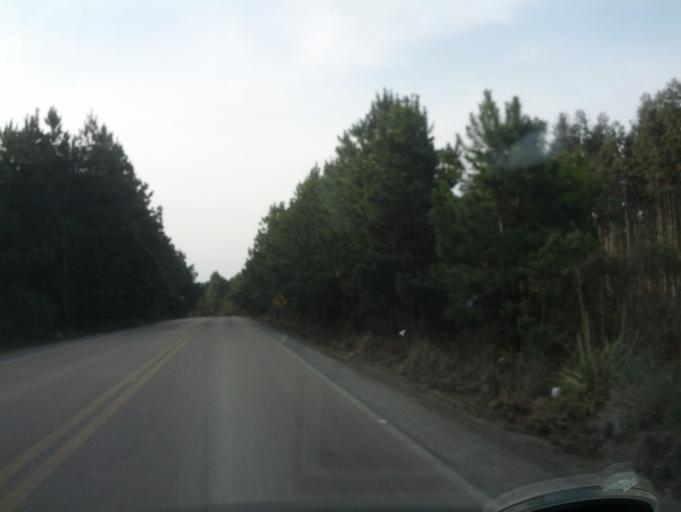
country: BR
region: Santa Catarina
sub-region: Otacilio Costa
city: Otacilio Costa
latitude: -27.4284
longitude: -50.1216
